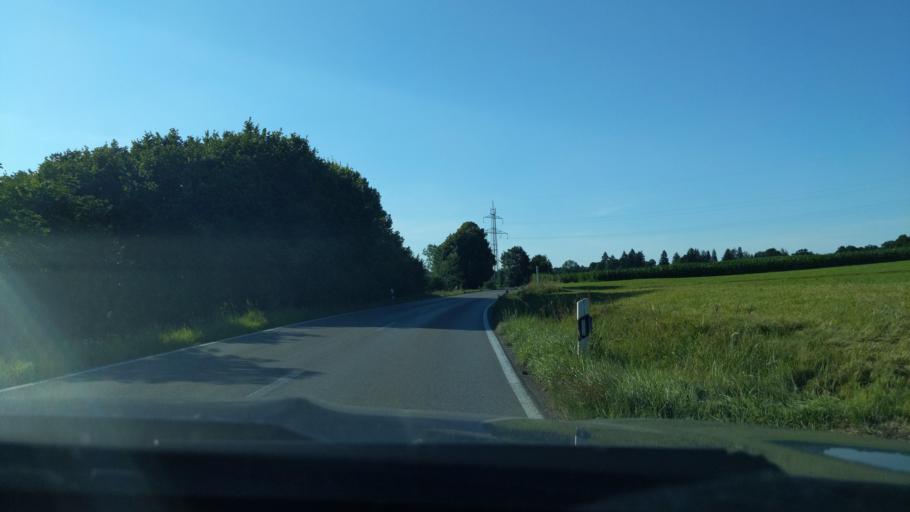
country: DE
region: Bavaria
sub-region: Upper Bavaria
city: Grafing bei Munchen
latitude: 48.0153
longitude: 11.9671
